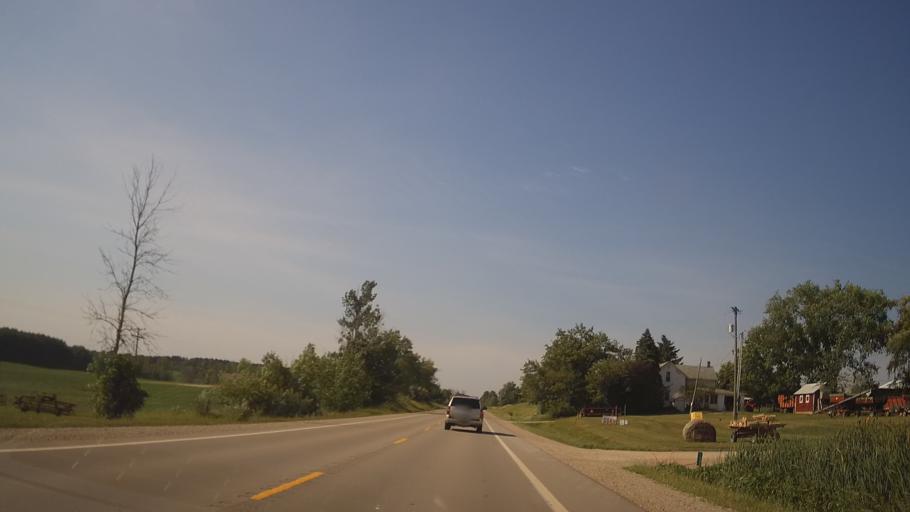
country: US
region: Michigan
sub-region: Ogemaw County
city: West Branch
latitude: 44.2874
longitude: -84.1257
